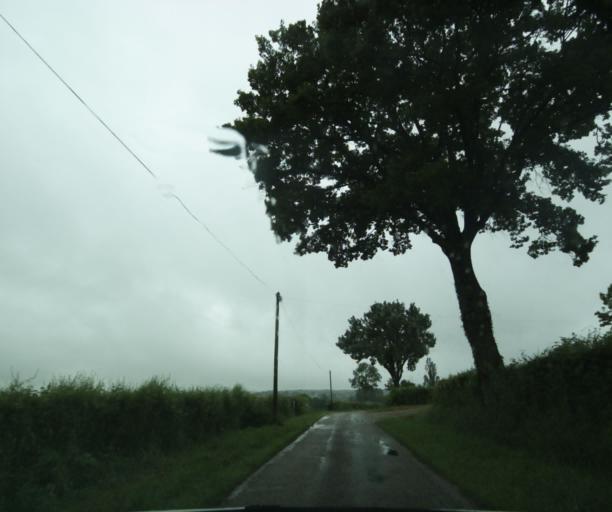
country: FR
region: Bourgogne
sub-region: Departement de Saone-et-Loire
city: Paray-le-Monial
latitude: 46.4762
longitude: 4.1799
